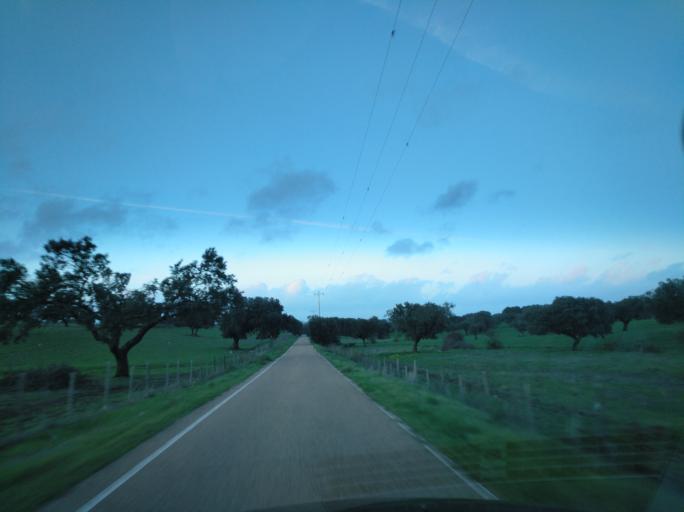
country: PT
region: Portalegre
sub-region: Campo Maior
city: Campo Maior
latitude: 39.0783
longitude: -7.1164
